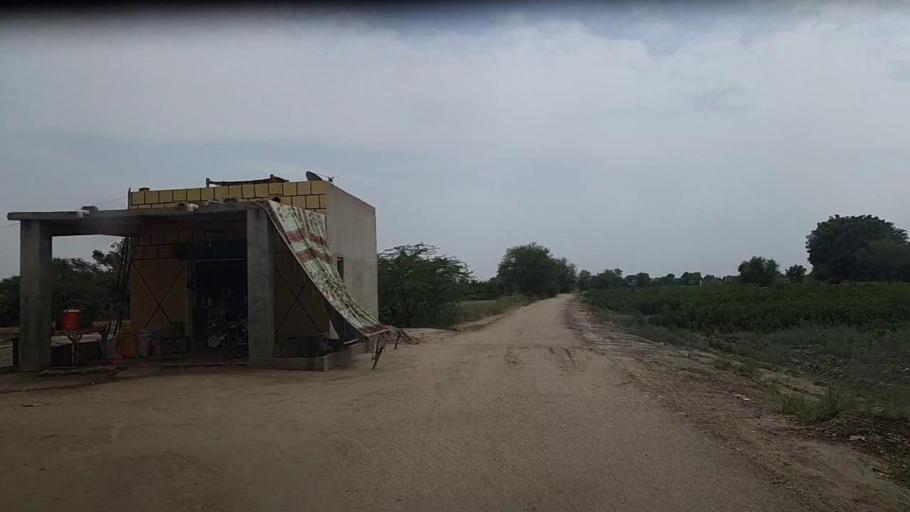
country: PK
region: Sindh
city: Pad Idan
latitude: 26.8795
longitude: 68.2954
